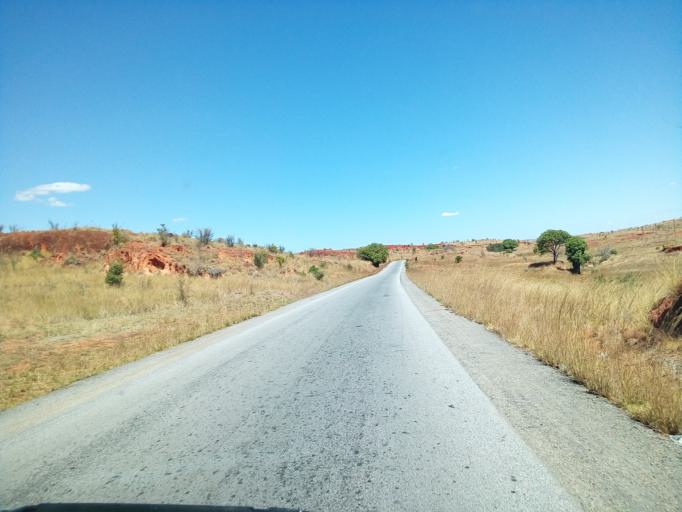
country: MG
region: Betsiboka
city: Maevatanana
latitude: -17.0873
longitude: 46.8128
